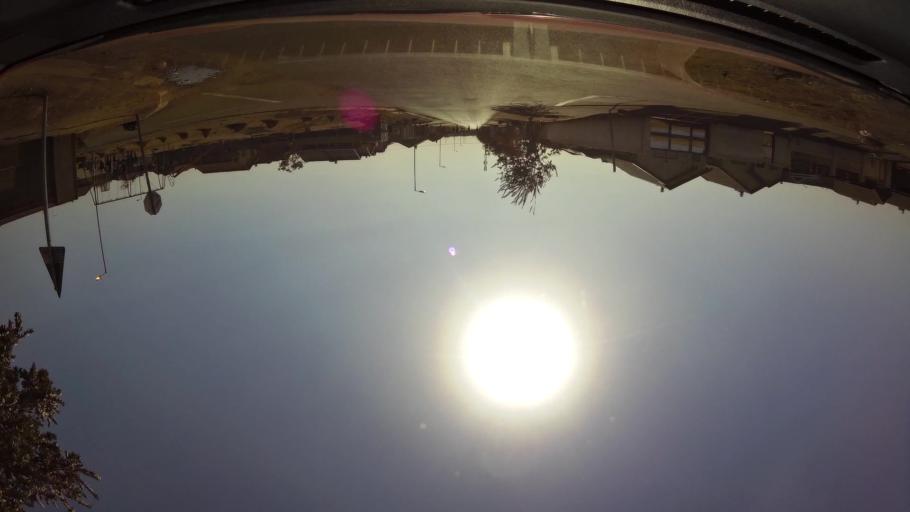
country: ZA
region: Gauteng
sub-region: City of Tshwane Metropolitan Municipality
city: Mabopane
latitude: -25.5734
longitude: 28.0980
